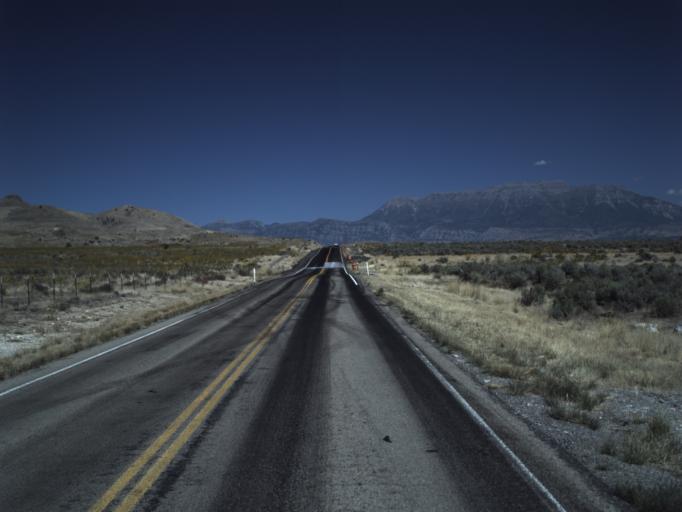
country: US
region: Utah
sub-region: Utah County
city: Saratoga Springs
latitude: 40.2076
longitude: -111.8937
